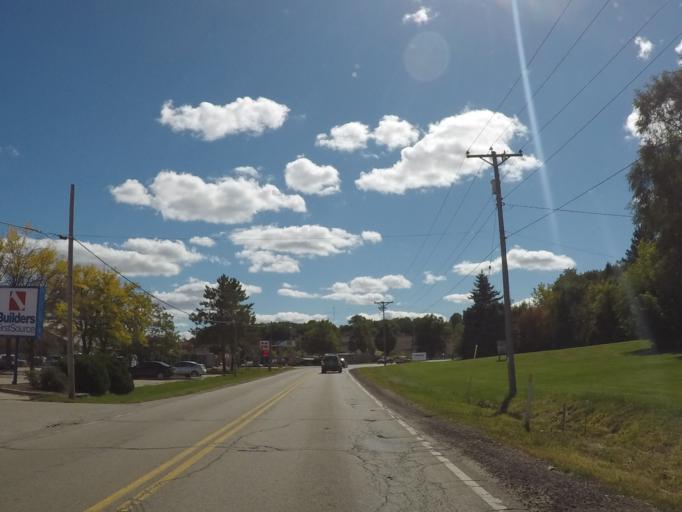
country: US
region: Wisconsin
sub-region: Dane County
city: Middleton
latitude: 43.0949
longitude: -89.5347
